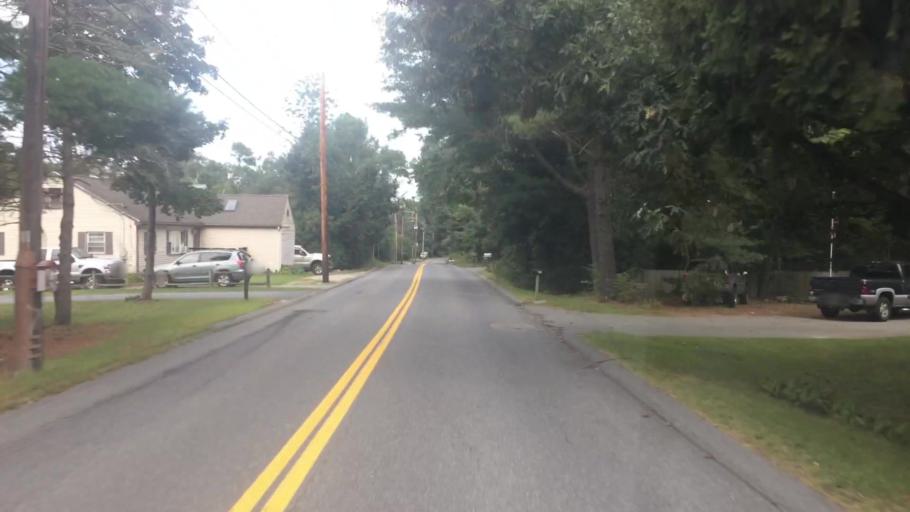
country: US
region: Massachusetts
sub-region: Middlesex County
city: West Concord
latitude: 42.4600
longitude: -71.4150
